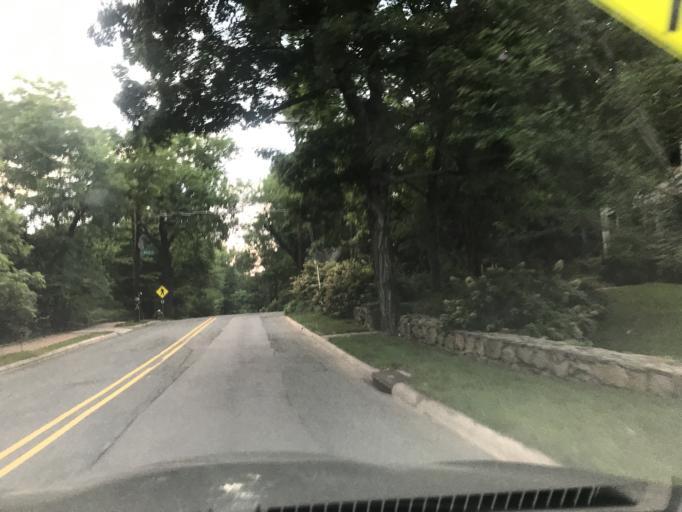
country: US
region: North Carolina
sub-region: Orange County
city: Chapel Hill
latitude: 35.9173
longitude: -79.0502
